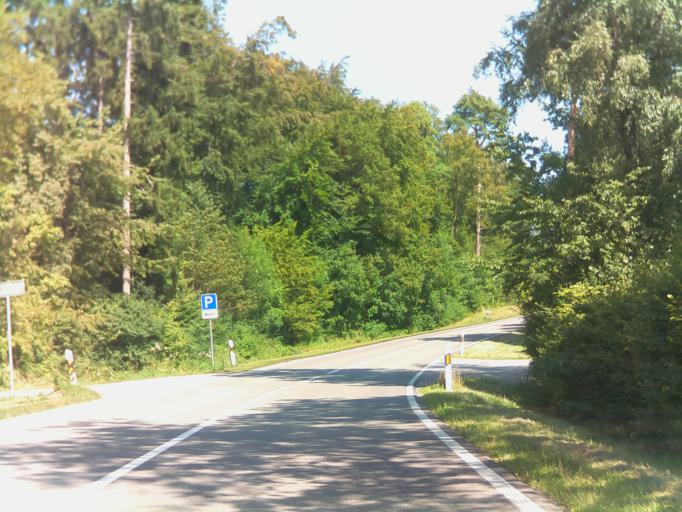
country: DE
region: Baden-Wuerttemberg
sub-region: Regierungsbezirk Stuttgart
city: Rutesheim
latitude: 48.8222
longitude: 8.9540
